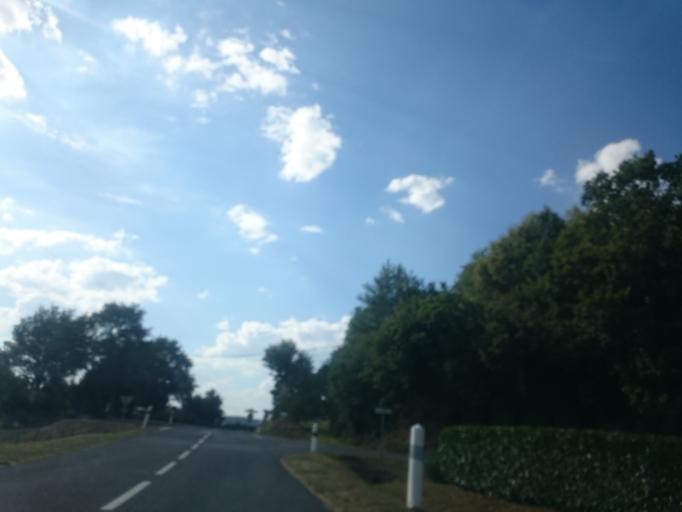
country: FR
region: Auvergne
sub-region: Departement du Cantal
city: Laroquebrou
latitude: 44.8889
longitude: 2.2108
